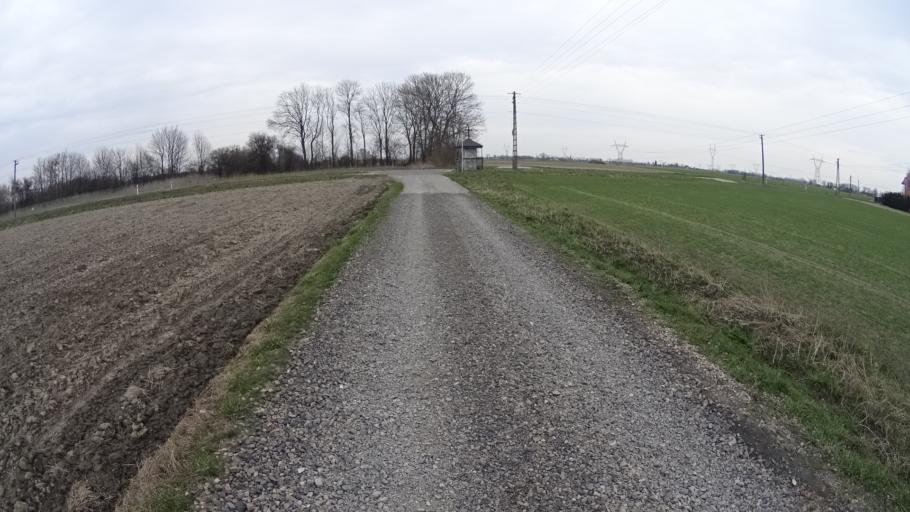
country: PL
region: Masovian Voivodeship
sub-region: Powiat warszawski zachodni
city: Jozefow
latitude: 52.2394
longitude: 20.6912
